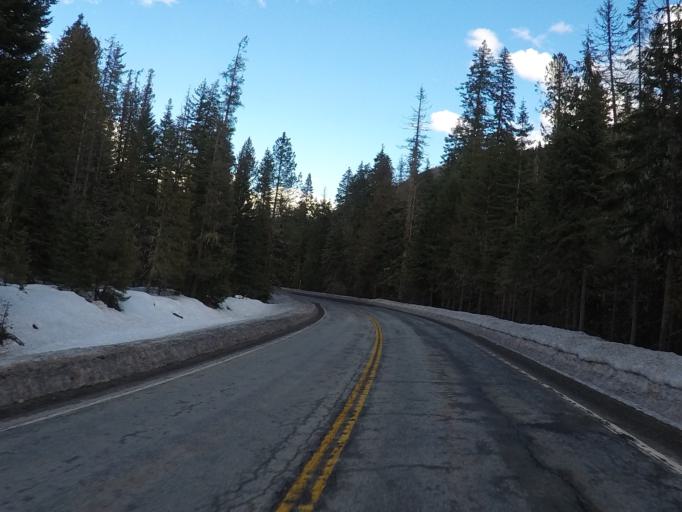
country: US
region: Montana
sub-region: Ravalli County
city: Hamilton
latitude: 46.5075
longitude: -114.7758
